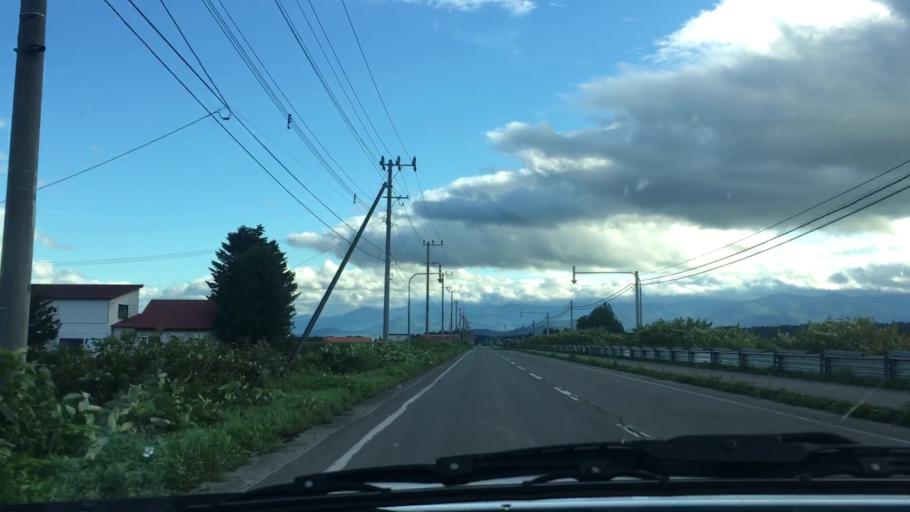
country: JP
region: Hokkaido
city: Otofuke
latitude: 43.1530
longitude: 142.9011
